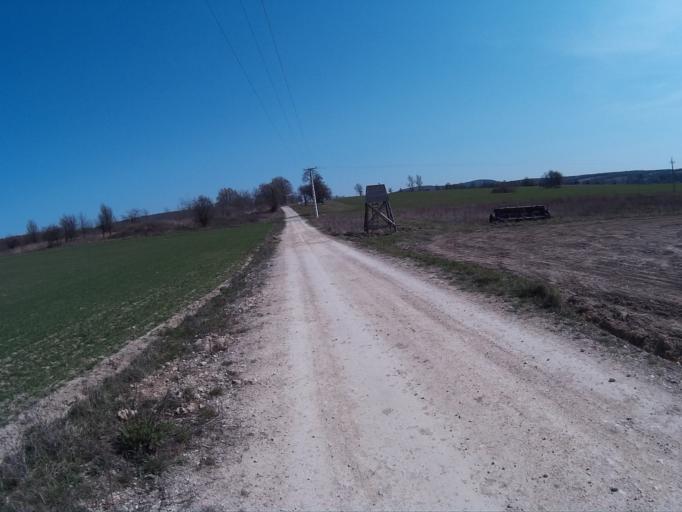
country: HU
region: Veszprem
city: Herend
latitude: 47.2045
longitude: 17.7835
